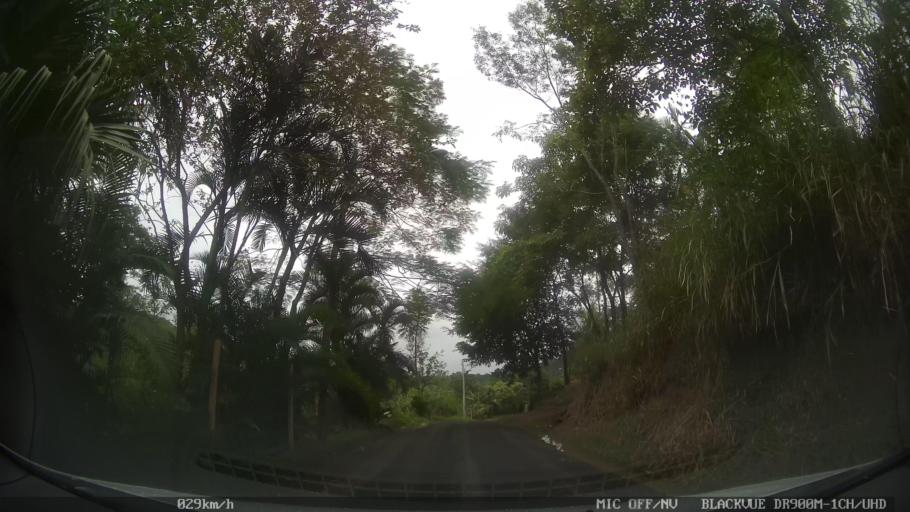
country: BR
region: Sao Paulo
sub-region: Cajati
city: Cajati
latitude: -24.7901
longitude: -48.1800
